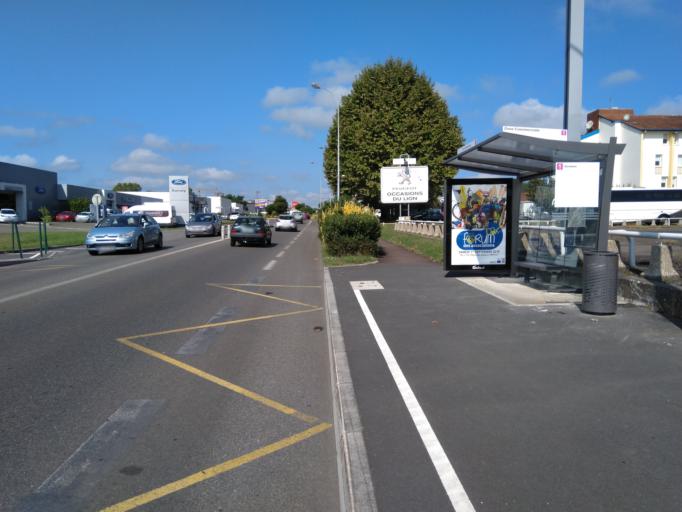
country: FR
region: Aquitaine
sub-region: Departement des Landes
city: Saint-Paul-les-Dax
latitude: 43.7265
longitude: -1.0762
